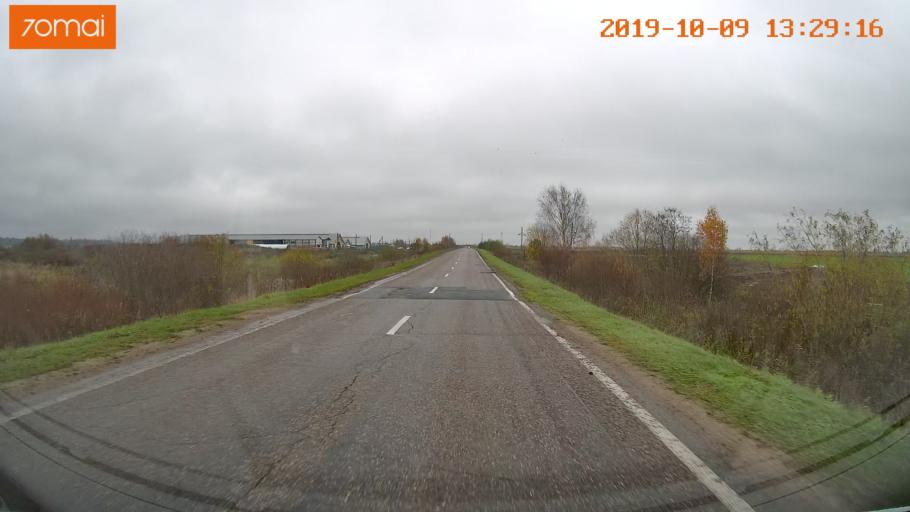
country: RU
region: Jaroslavl
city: Lyubim
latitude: 58.3150
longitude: 40.9853
